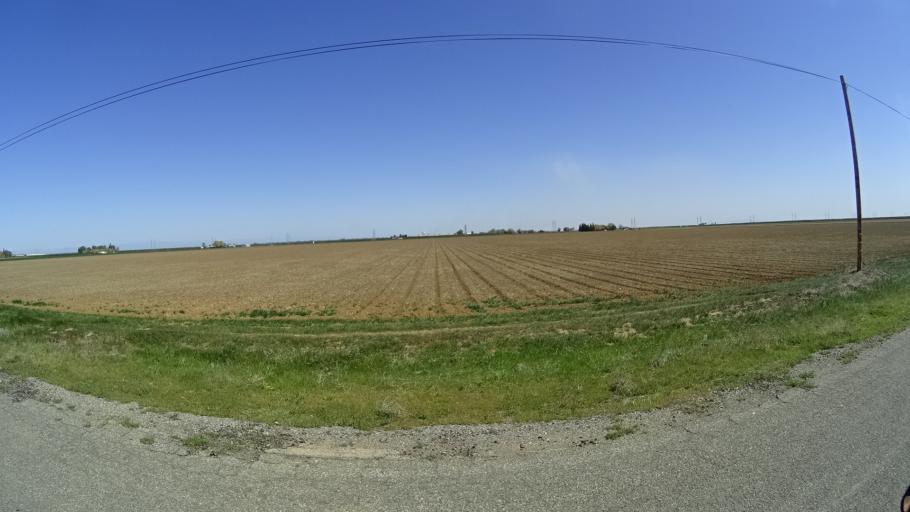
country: US
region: California
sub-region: Glenn County
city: Willows
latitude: 39.5156
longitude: -122.2774
